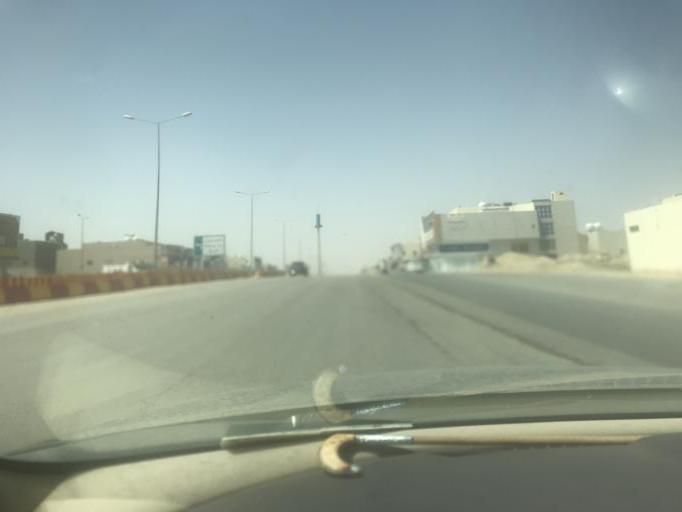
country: SA
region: Ar Riyad
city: Riyadh
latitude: 24.8107
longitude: 46.6005
